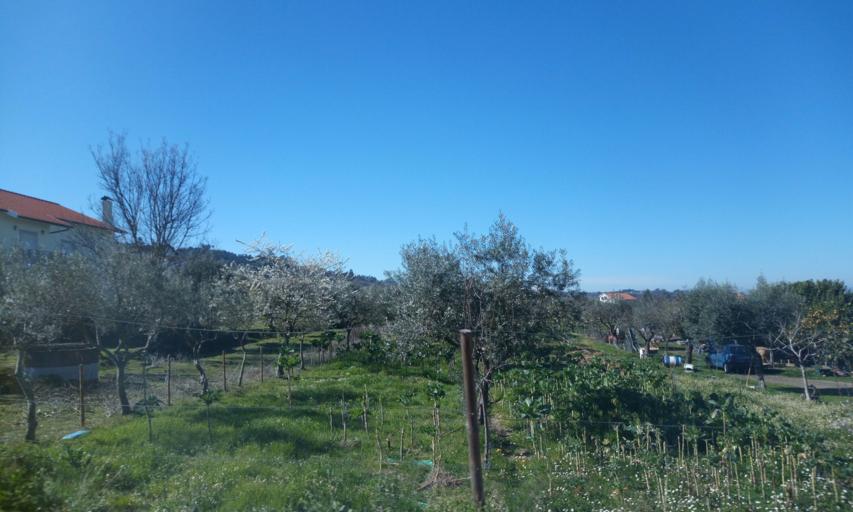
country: PT
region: Guarda
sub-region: Fornos de Algodres
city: Fornos de Algodres
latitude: 40.5223
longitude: -7.5521
